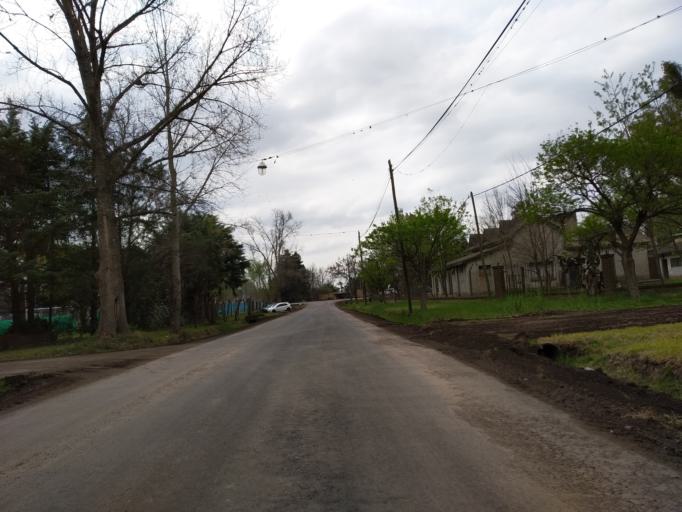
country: AR
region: Santa Fe
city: Funes
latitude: -32.9162
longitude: -60.8514
